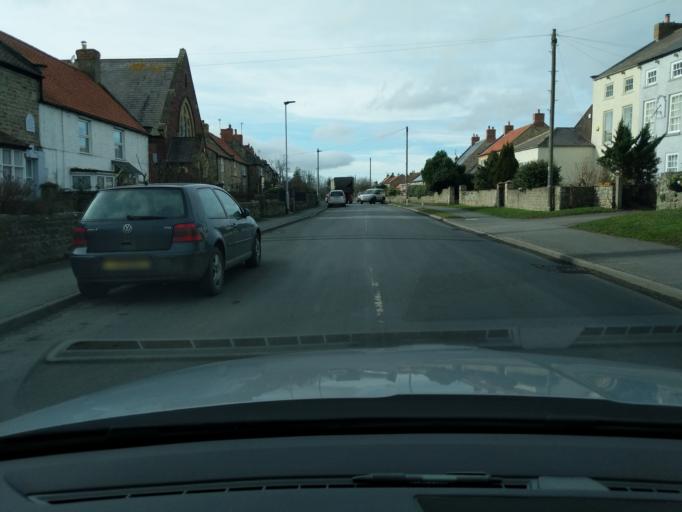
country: GB
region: England
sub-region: North Yorkshire
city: Catterick
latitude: 54.3922
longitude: -1.6657
